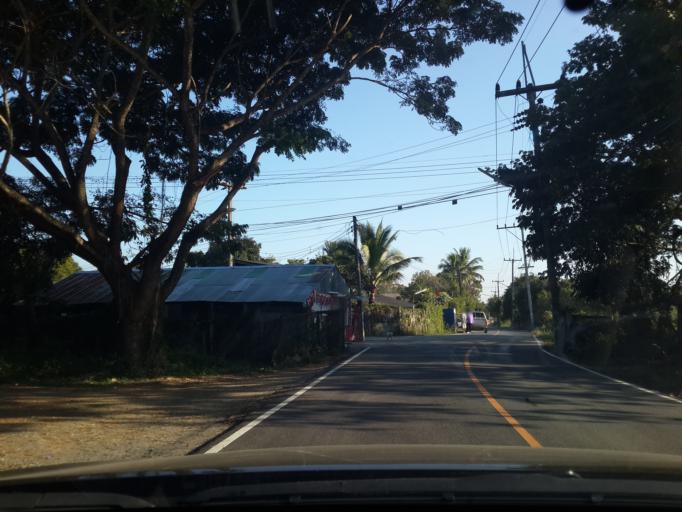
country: TH
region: Chiang Mai
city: San Sai
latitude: 18.9209
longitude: 99.1312
